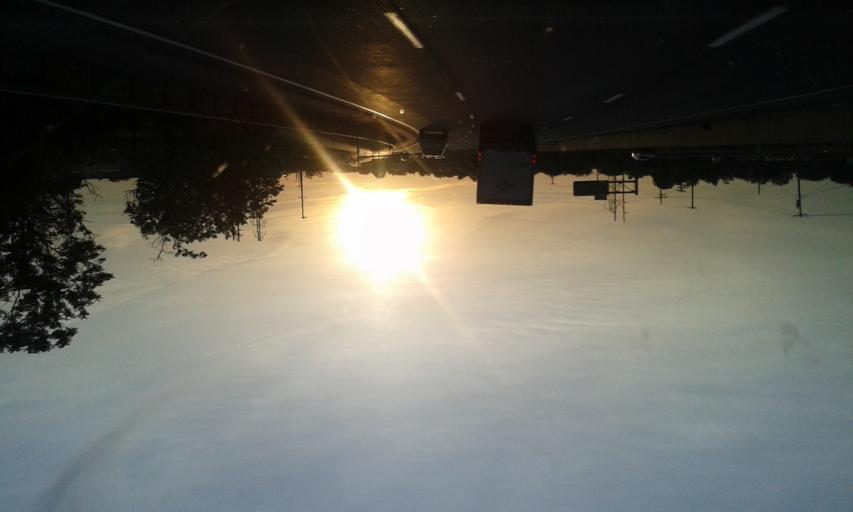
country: US
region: New York
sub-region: Onondaga County
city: Lakeland
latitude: 43.1068
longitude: -76.2536
